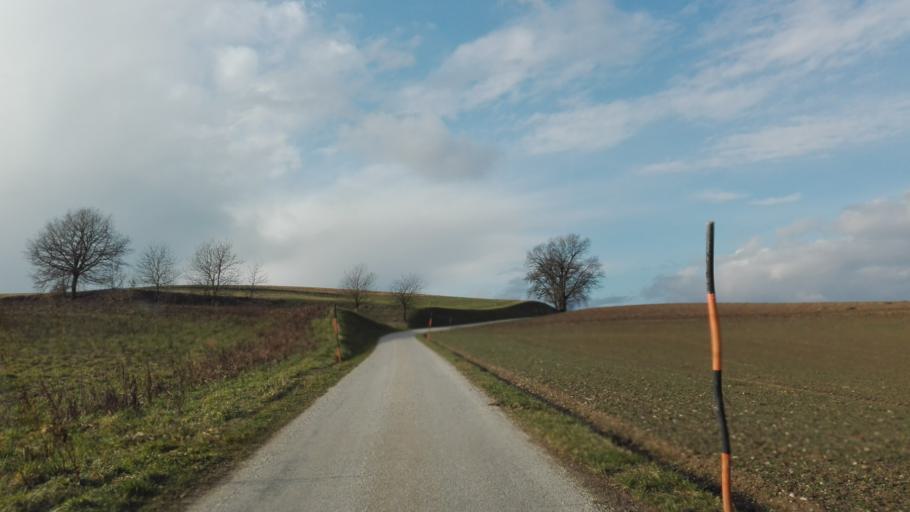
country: AT
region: Upper Austria
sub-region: Politischer Bezirk Perg
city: Perg
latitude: 48.2555
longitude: 14.6155
